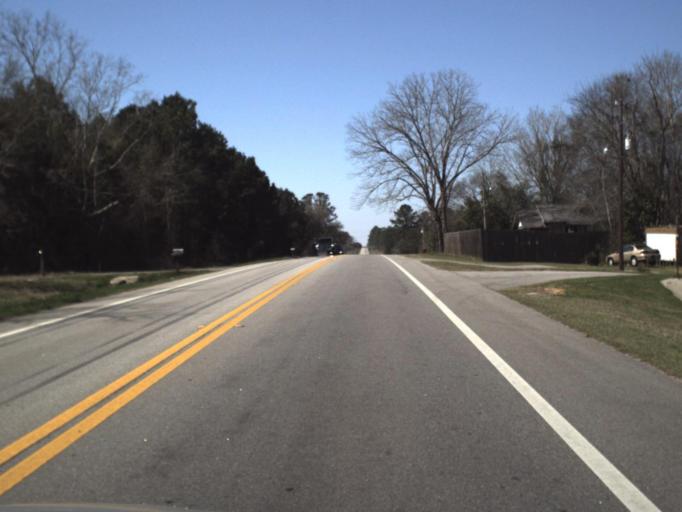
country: US
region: Florida
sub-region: Jackson County
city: Marianna
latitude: 30.8089
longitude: -85.2933
